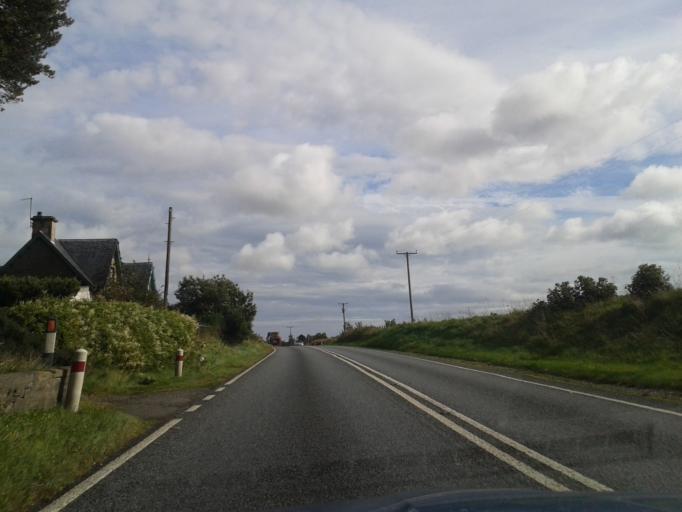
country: GB
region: Scotland
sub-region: Moray
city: Kinloss
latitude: 57.6204
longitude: -3.5641
